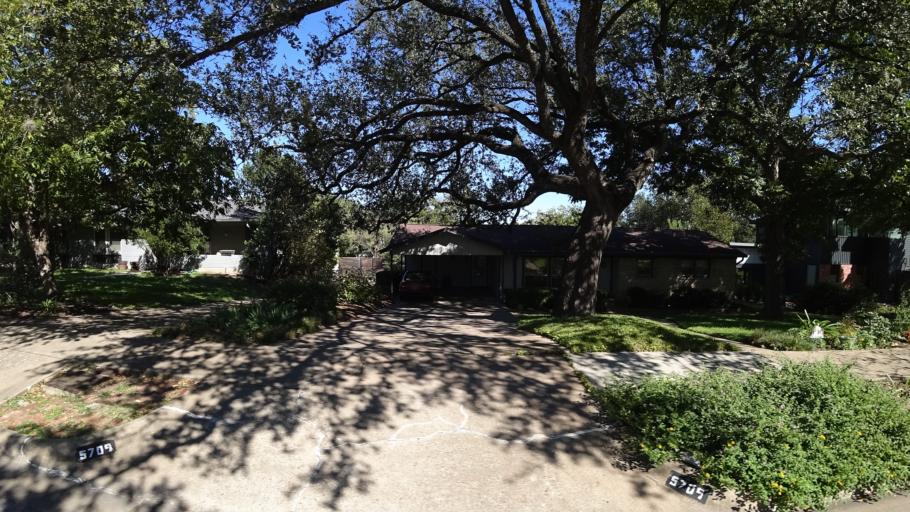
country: US
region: Texas
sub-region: Travis County
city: West Lake Hills
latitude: 30.3359
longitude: -97.7525
